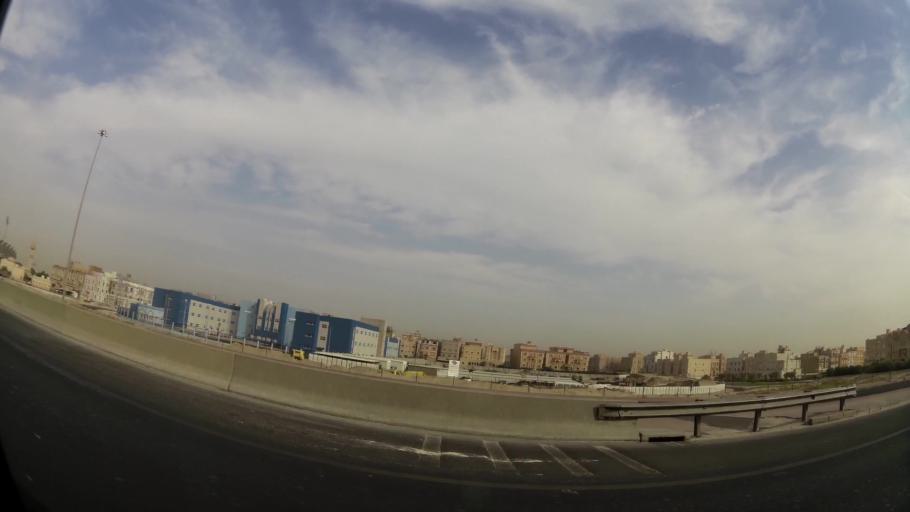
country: KW
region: Al Asimah
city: Ar Rabiyah
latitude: 29.2671
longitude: 47.9291
